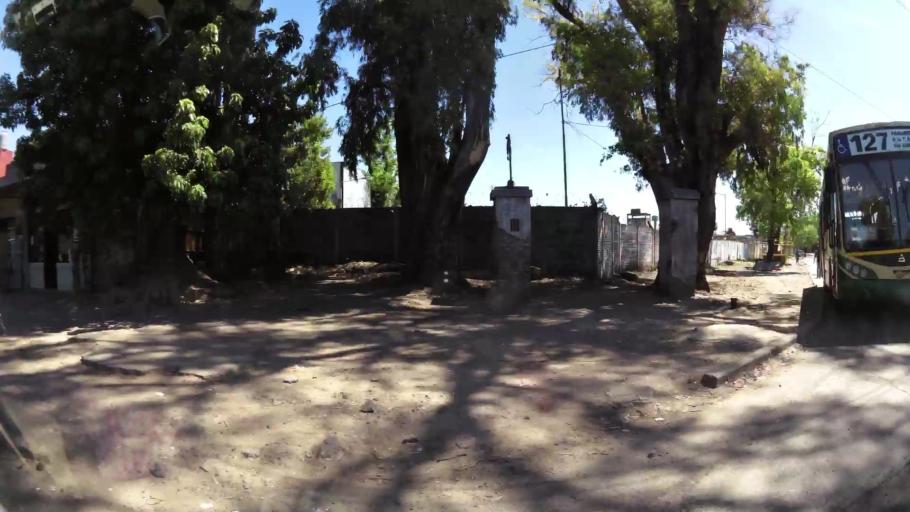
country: AR
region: Buenos Aires
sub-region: Partido de Tigre
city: Tigre
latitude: -34.5069
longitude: -58.5810
